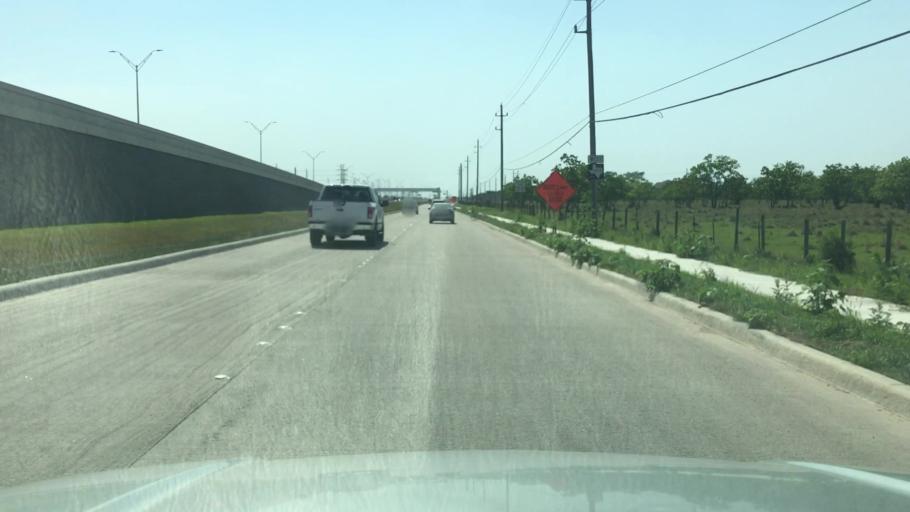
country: US
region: Texas
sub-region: Fort Bend County
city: Cinco Ranch
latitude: 29.6991
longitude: -95.7938
